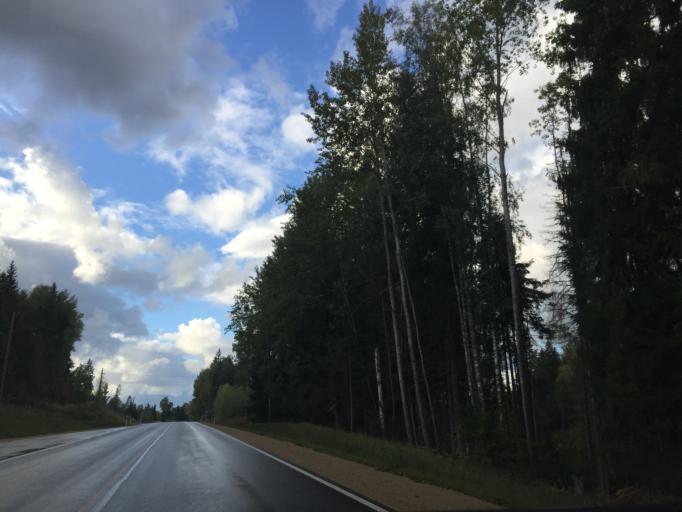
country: LV
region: Ligatne
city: Ligatne
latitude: 57.1597
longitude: 25.0592
